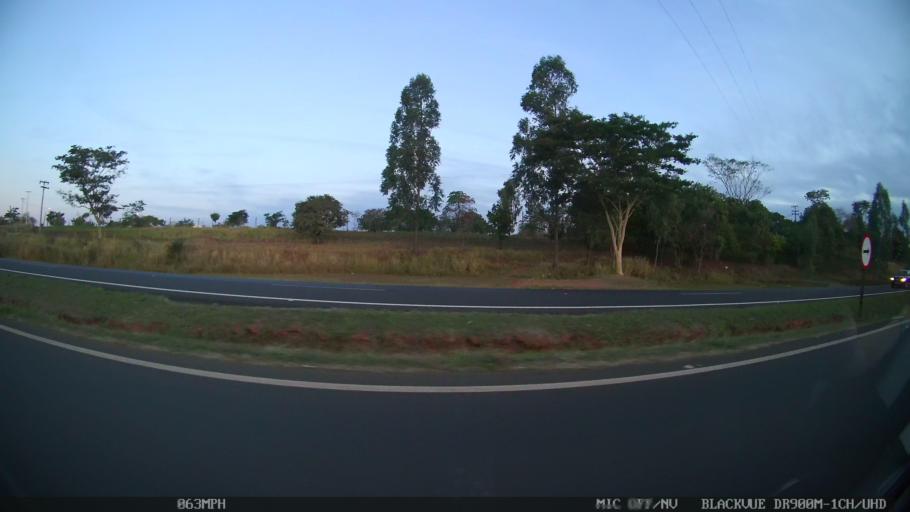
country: BR
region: Sao Paulo
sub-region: Catanduva
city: Catanduva
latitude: -21.1112
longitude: -48.9685
